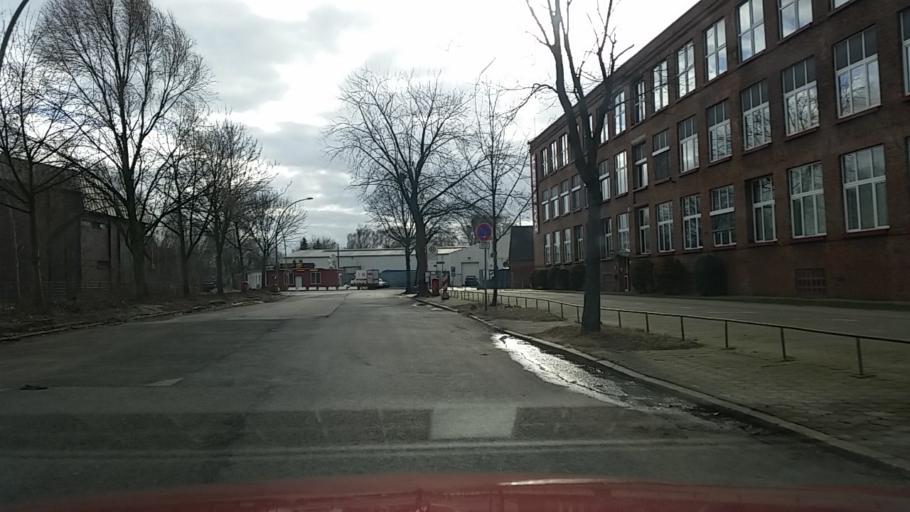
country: DE
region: Hamburg
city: Rothenburgsort
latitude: 53.5251
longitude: 10.0258
